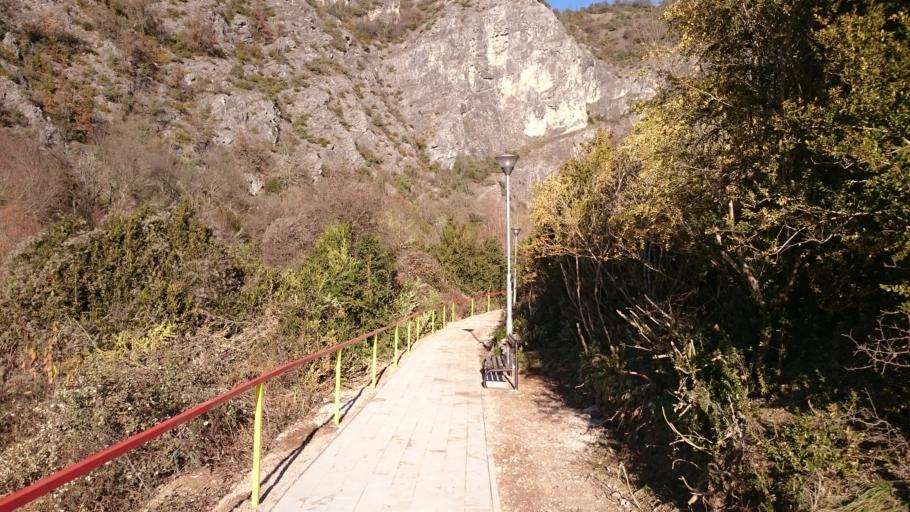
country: MK
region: Makedonski Brod
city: Makedonski Brod
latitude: 41.5466
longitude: 21.2507
